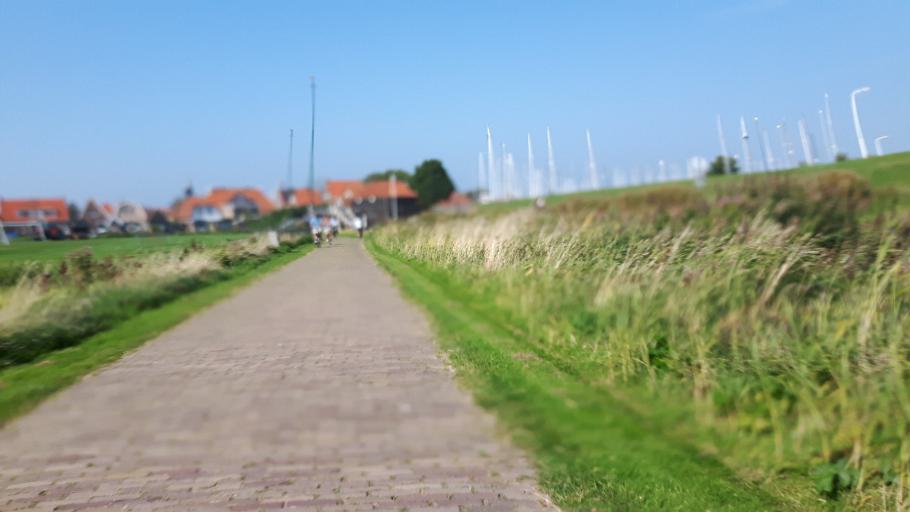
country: NL
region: Friesland
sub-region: Sudwest Fryslan
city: Koudum
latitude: 52.9421
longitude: 5.4054
